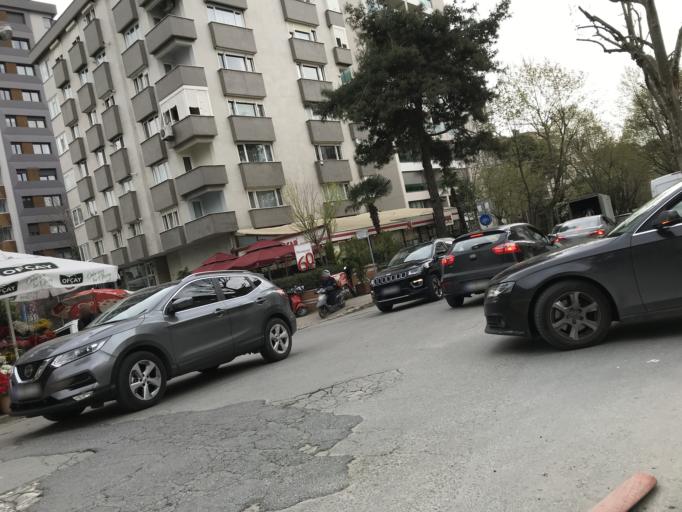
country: TR
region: Istanbul
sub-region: Atasehir
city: Atasehir
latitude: 40.9760
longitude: 29.0642
